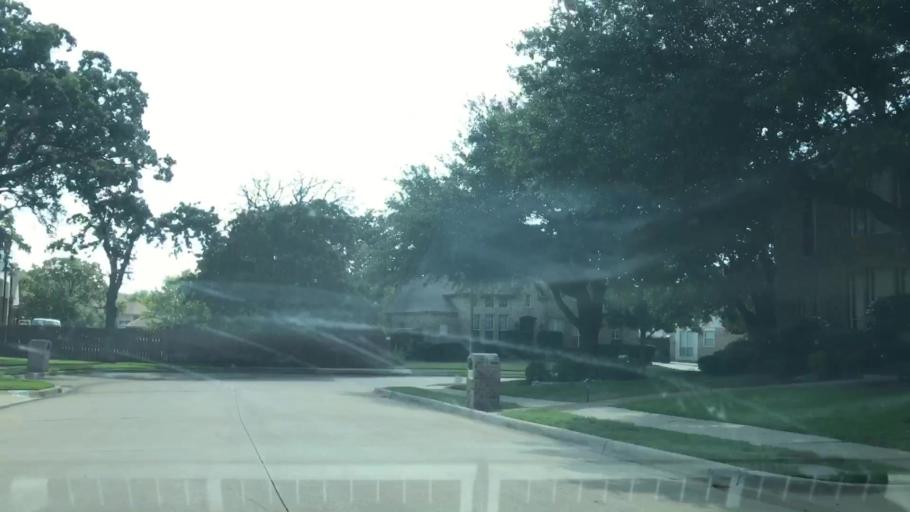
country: US
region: Texas
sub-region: Tarrant County
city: Keller
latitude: 32.9083
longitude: -97.2336
